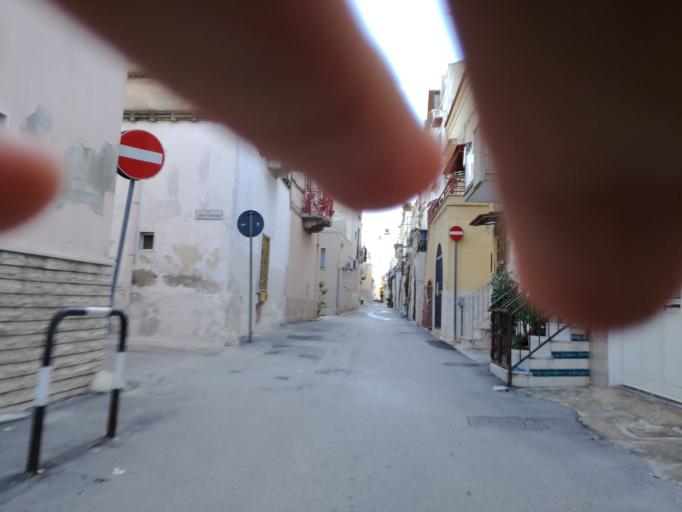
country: IT
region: Apulia
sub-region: Provincia di Bari
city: Adelfia
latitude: 41.0056
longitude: 16.8669
